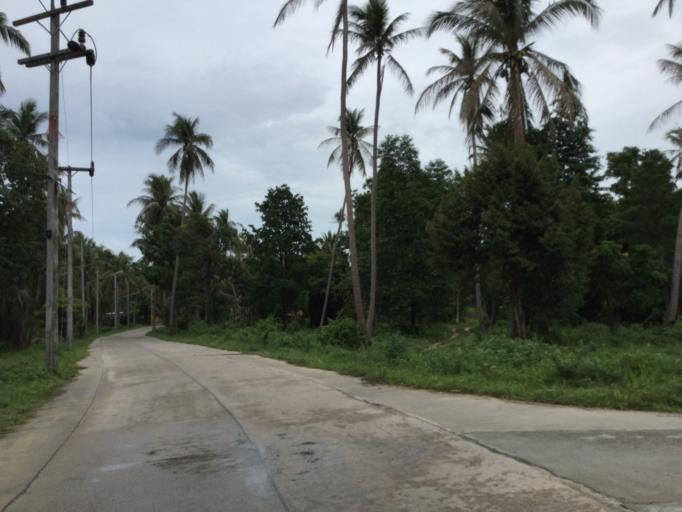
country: TH
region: Surat Thani
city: Ko Pha-Ngan
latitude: 9.7217
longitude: 100.0067
